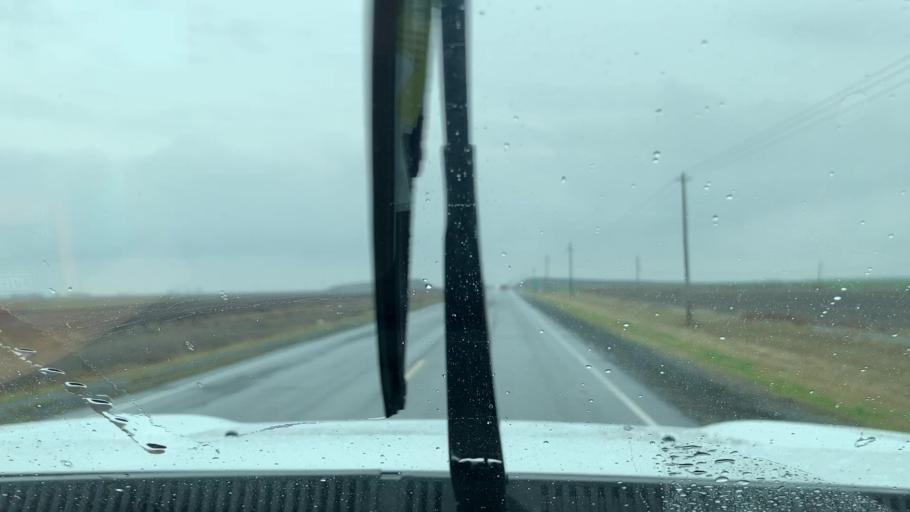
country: US
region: California
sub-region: Tulare County
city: Alpaugh
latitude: 35.9402
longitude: -119.4409
